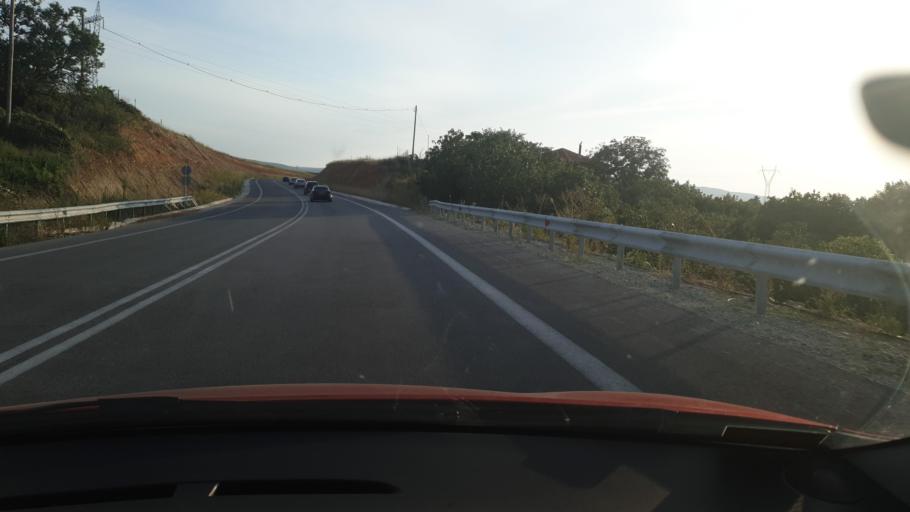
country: GR
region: Central Macedonia
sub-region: Nomos Chalkidikis
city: Galatista
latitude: 40.4651
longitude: 23.2296
